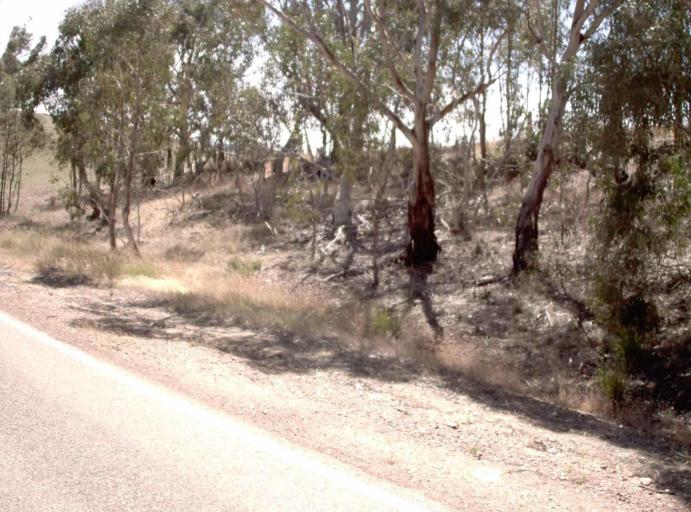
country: AU
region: Victoria
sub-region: Alpine
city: Mount Beauty
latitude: -37.0468
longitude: 147.6222
